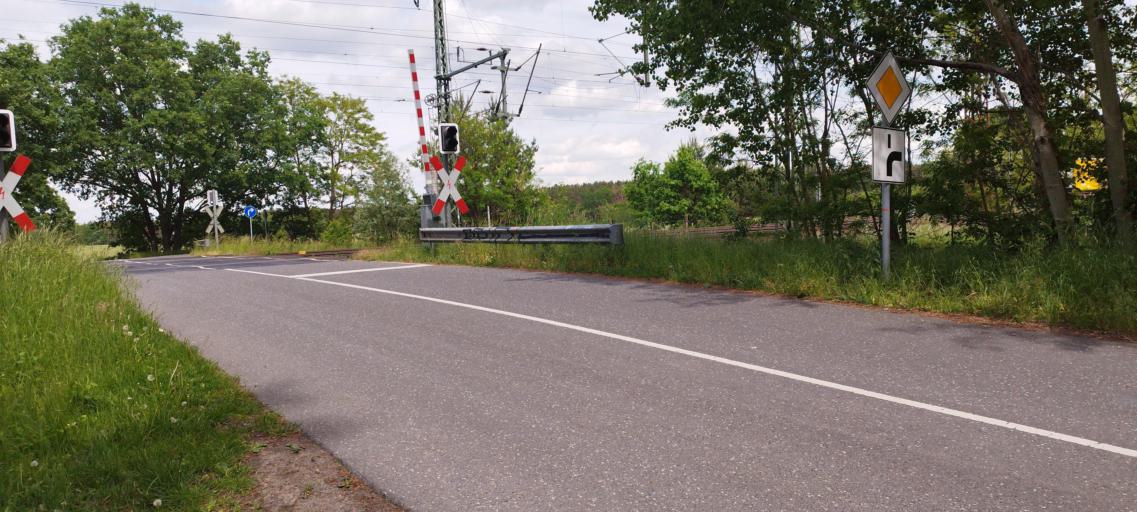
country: DE
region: Brandenburg
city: Berkenbruck
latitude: 52.3578
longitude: 14.1513
